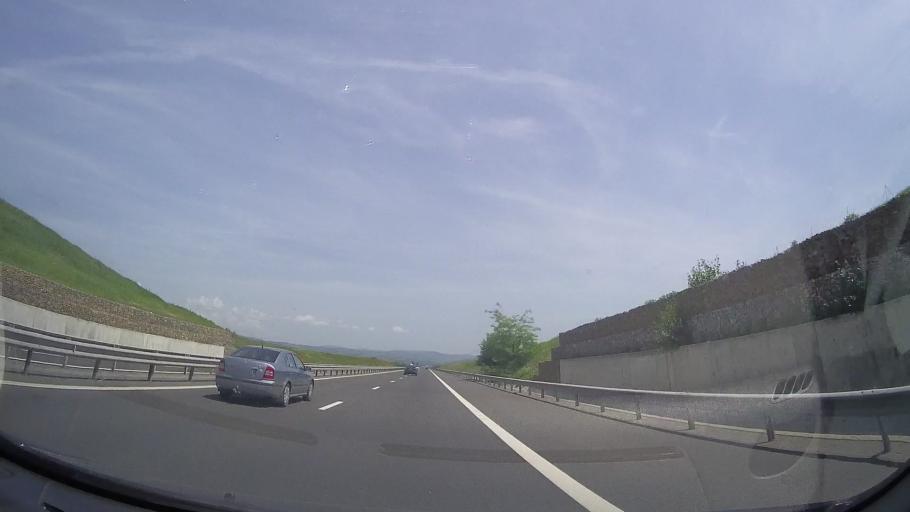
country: RO
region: Hunedoara
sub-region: Comuna Turdas
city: Turdas
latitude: 45.8514
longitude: 23.1368
